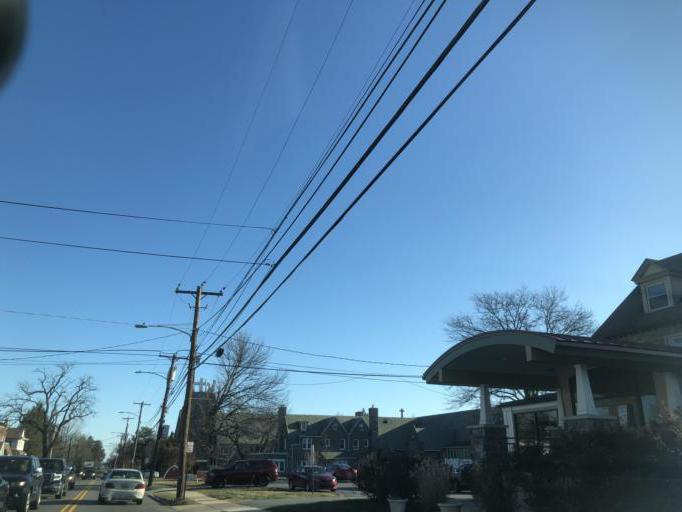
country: US
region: Pennsylvania
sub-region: Delaware County
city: Drexel Hill
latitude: 39.9466
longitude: -75.2925
